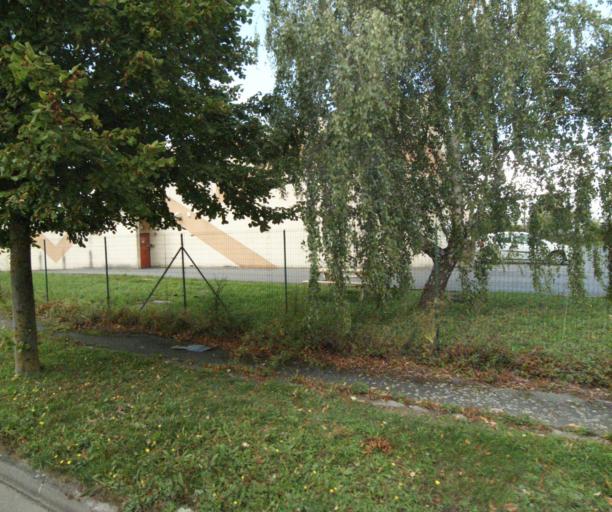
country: FR
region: Nord-Pas-de-Calais
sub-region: Departement du Nord
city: Lomme
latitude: 50.6379
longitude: 2.9794
